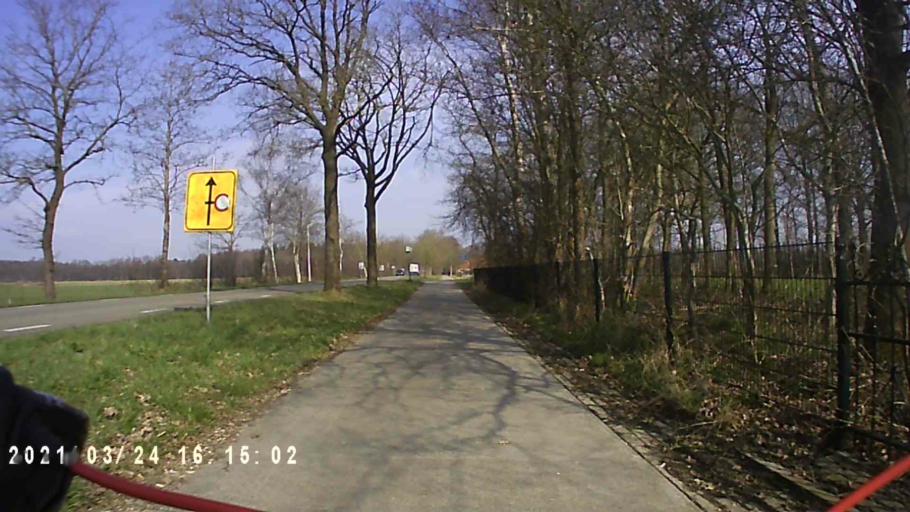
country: NL
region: Friesland
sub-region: Gemeente Heerenveen
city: Jubbega
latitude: 53.0431
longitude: 6.2354
